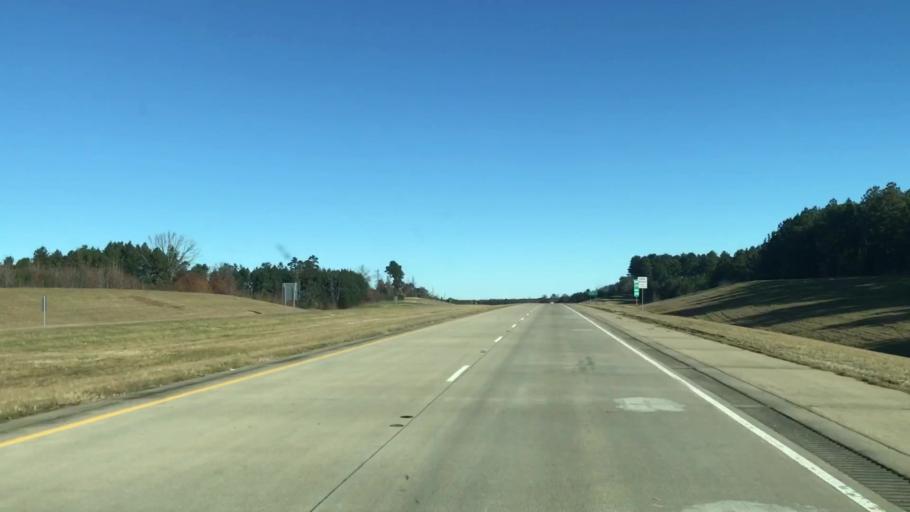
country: US
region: Louisiana
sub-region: Caddo Parish
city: Vivian
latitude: 33.0092
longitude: -93.9045
